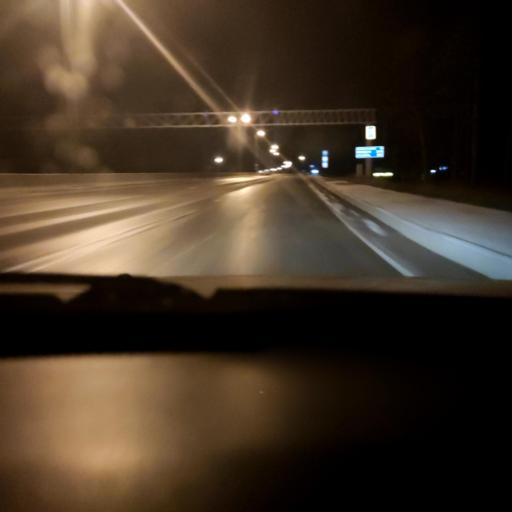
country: RU
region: Perm
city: Kondratovo
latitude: 58.0419
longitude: 56.0377
